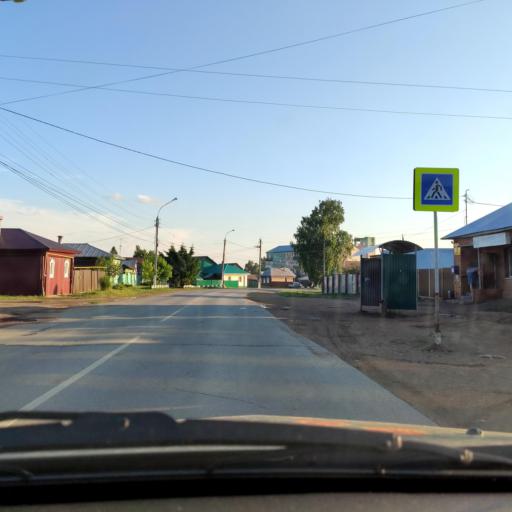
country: RU
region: Bashkortostan
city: Blagoveshchensk
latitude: 55.0330
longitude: 55.9898
